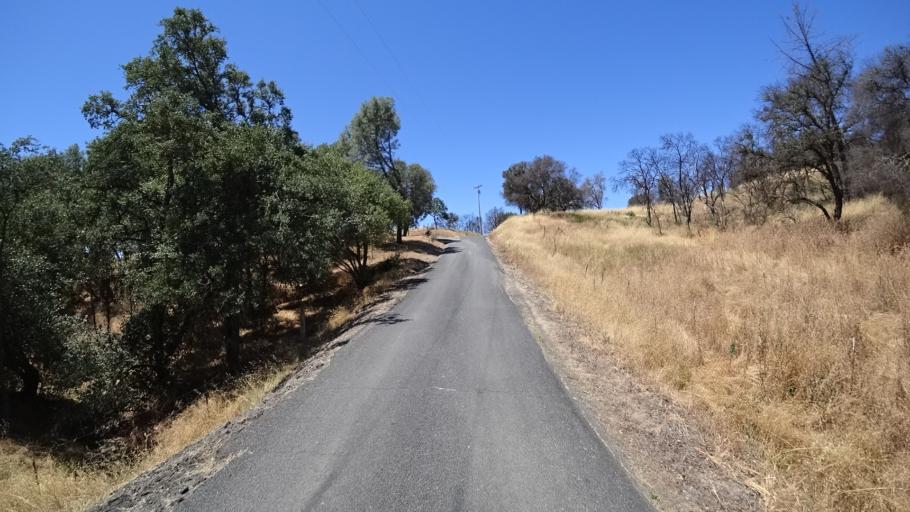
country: US
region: California
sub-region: Calaveras County
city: Copperopolis
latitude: 37.9654
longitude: -120.6950
